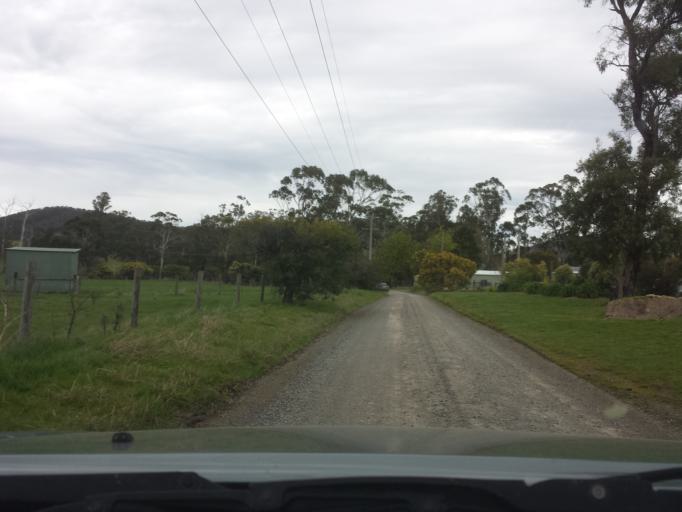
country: AU
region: Victoria
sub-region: Yarra Ranges
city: Yarra Glen
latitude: -37.5795
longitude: 145.3804
